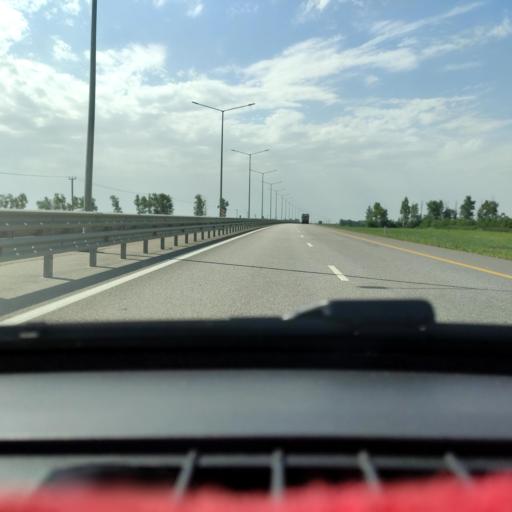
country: RU
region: Voronezj
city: Podkletnoye
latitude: 51.5272
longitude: 39.5100
